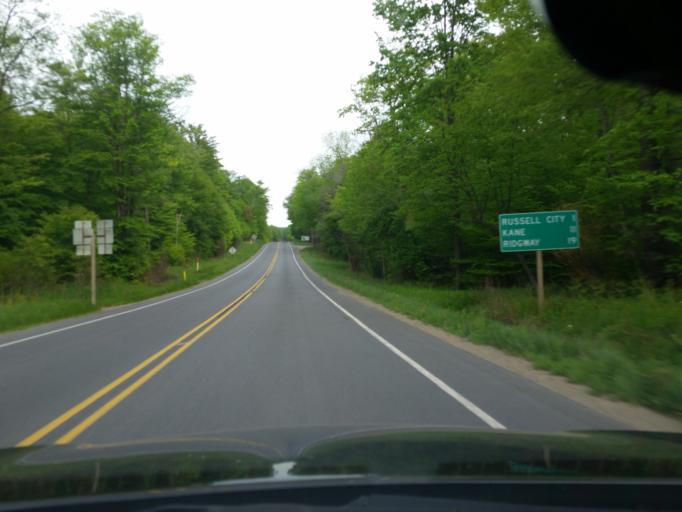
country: US
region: Pennsylvania
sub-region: McKean County
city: Kane
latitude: 41.5791
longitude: -78.9298
